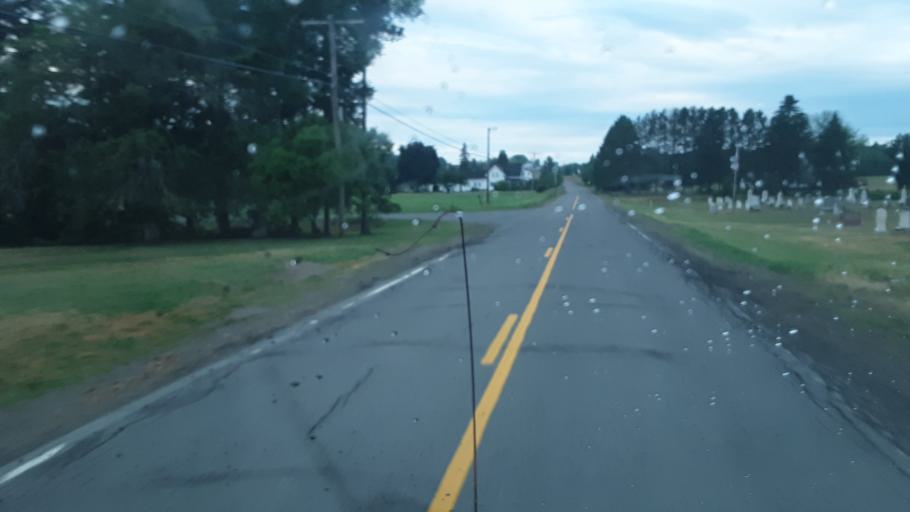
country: US
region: Maine
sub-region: Aroostook County
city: Presque Isle
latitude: 46.7334
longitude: -68.1793
